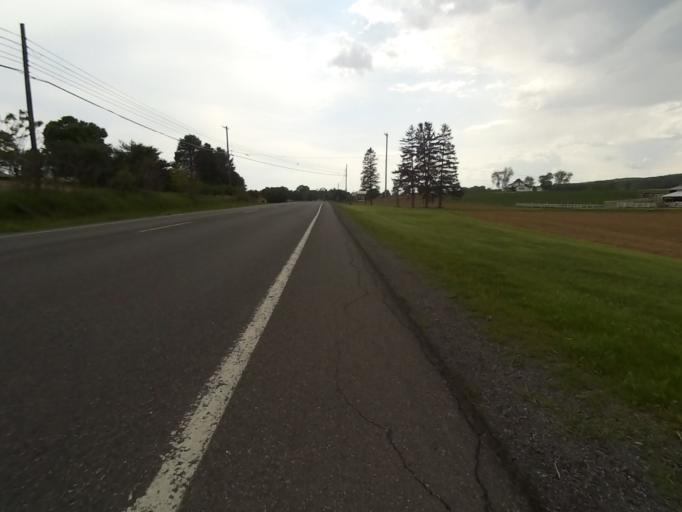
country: US
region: Pennsylvania
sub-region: Centre County
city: Zion
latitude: 40.9484
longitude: -77.6305
